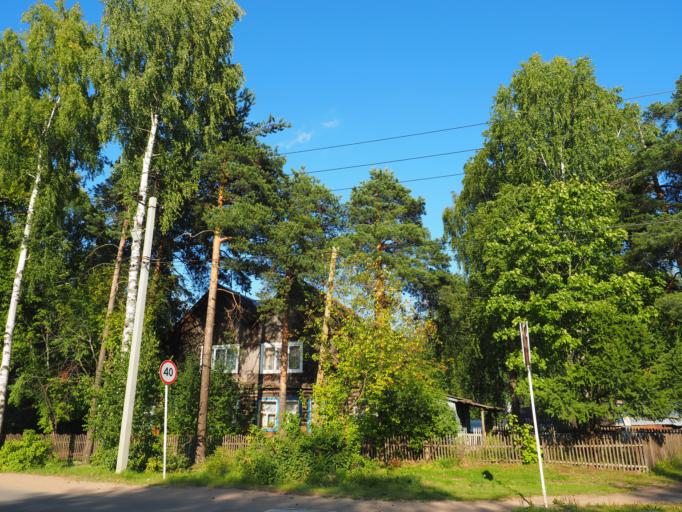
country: RU
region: Vologda
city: Chagoda
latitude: 59.1676
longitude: 35.3324
